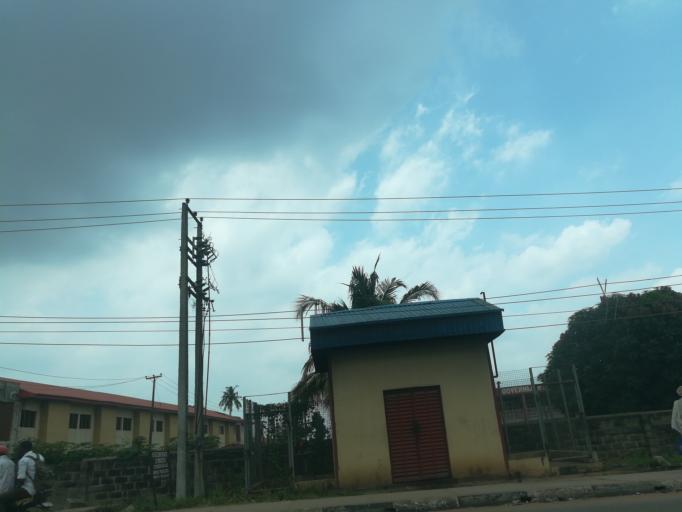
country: NG
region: Lagos
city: Ikorodu
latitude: 6.6194
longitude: 3.5175
